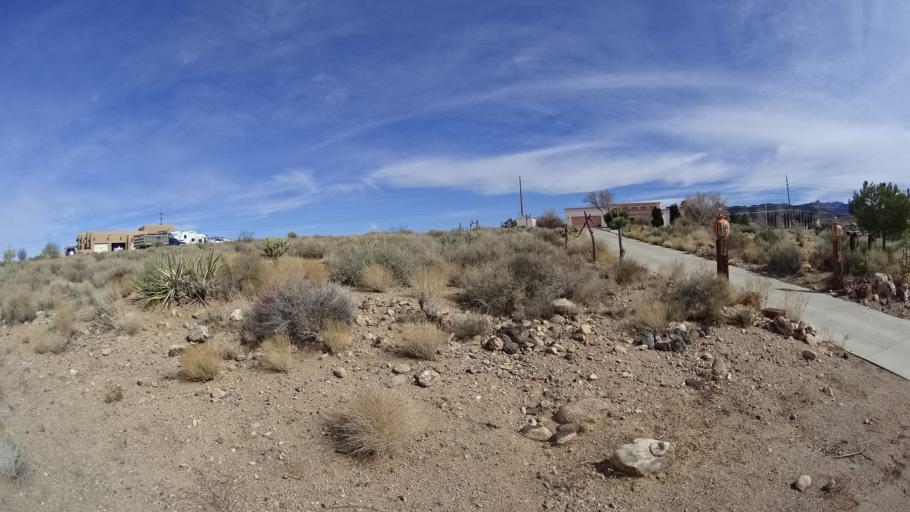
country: US
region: Arizona
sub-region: Mohave County
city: Kingman
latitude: 35.1904
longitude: -113.9868
